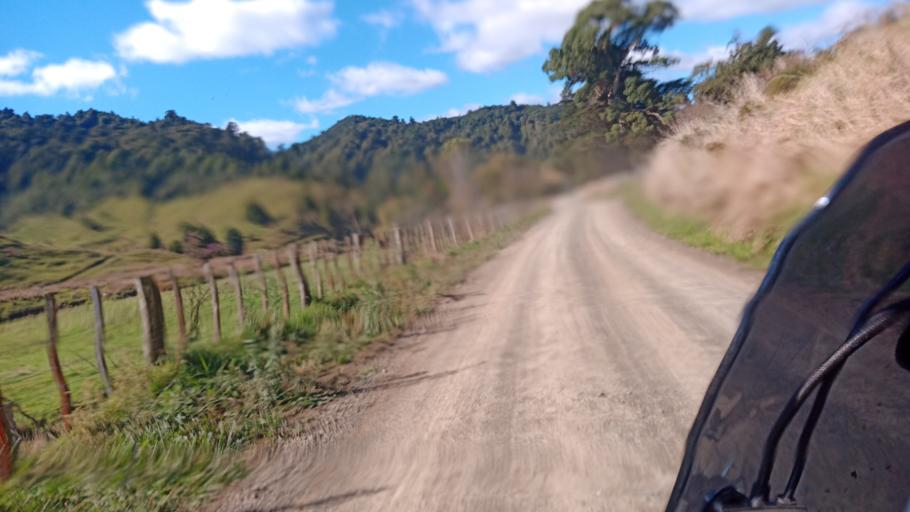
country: NZ
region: Bay of Plenty
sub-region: Opotiki District
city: Opotiki
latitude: -38.2515
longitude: 177.5838
